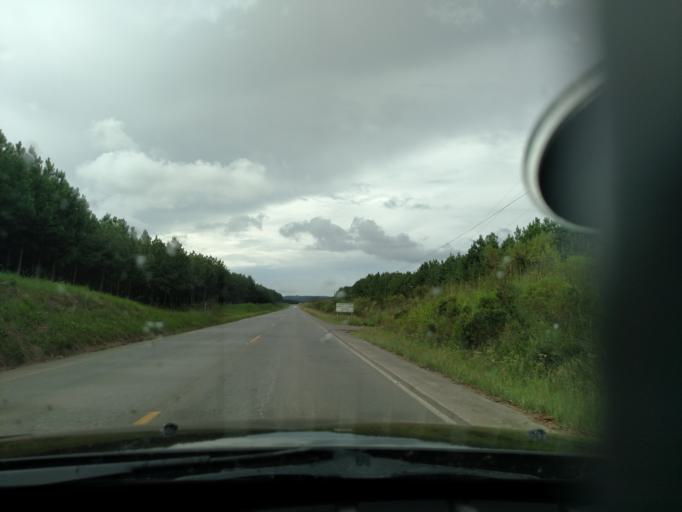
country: BR
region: Santa Catarina
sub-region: Lages
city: Lages
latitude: -27.7510
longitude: -50.1979
